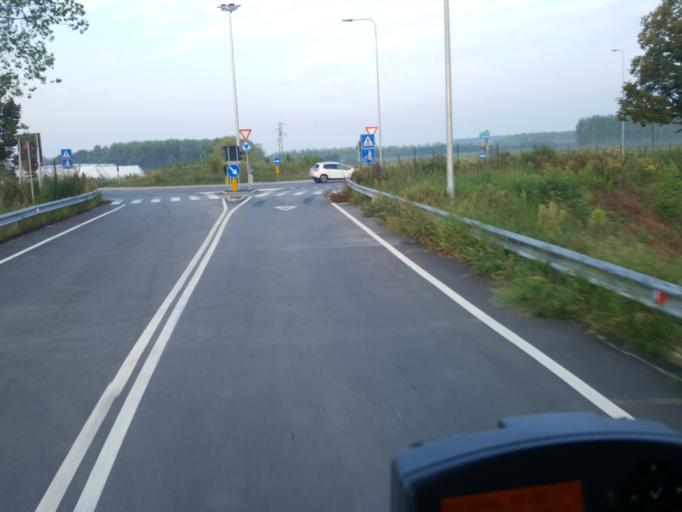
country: IT
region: Piedmont
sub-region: Provincia di Torino
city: Torrazza Piemonte
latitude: 45.2302
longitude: 7.9762
